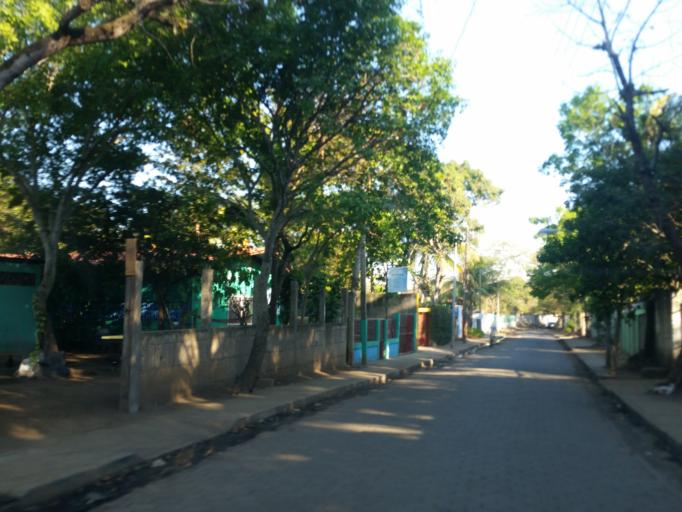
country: NI
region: Masaya
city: Ticuantepe
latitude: 12.0735
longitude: -86.2148
